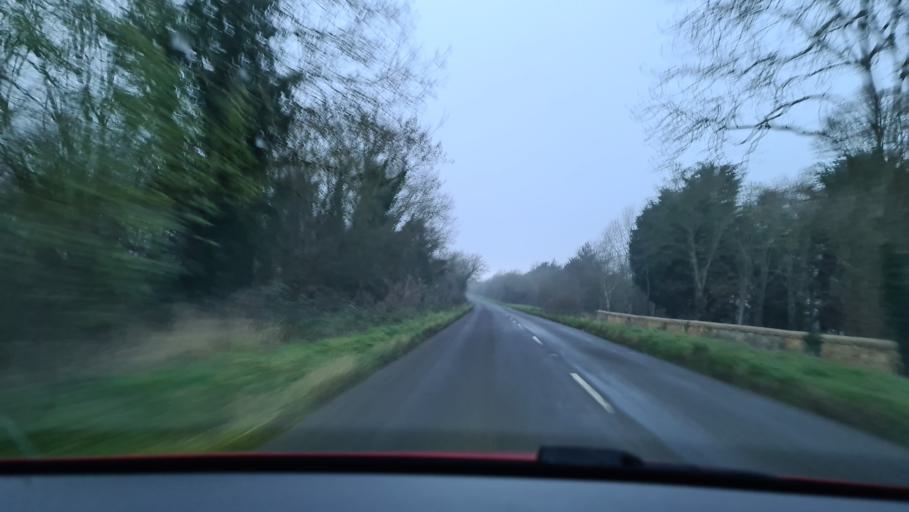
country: GB
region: England
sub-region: Oxfordshire
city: Bicester
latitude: 51.8919
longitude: -1.2000
